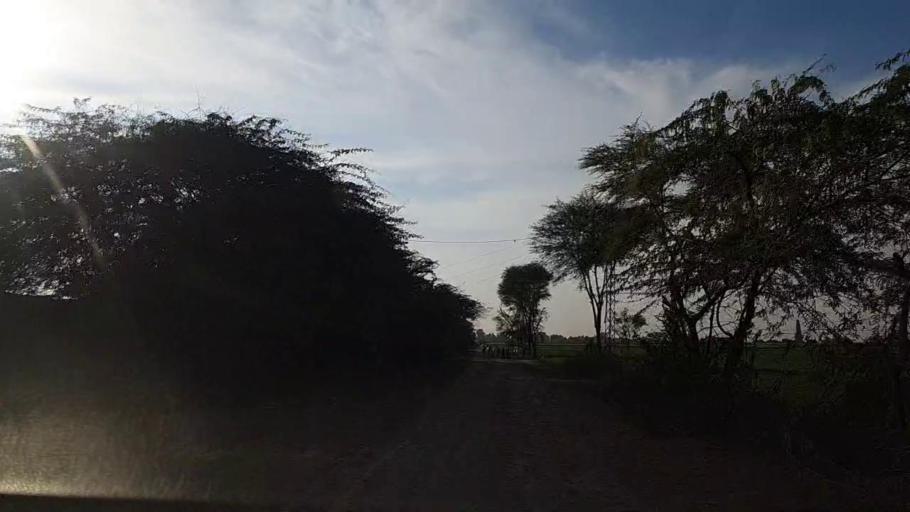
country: PK
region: Sindh
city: Bandhi
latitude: 26.5535
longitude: 68.2445
